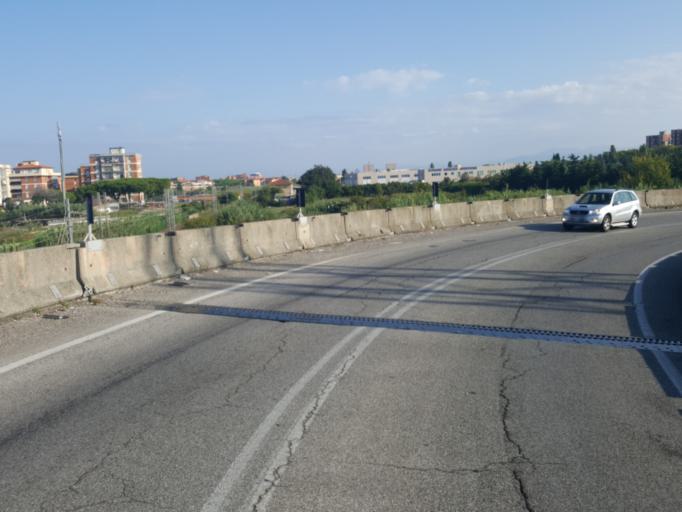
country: IT
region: Tuscany
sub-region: Provincia di Livorno
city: Livorno
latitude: 43.5337
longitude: 10.3327
